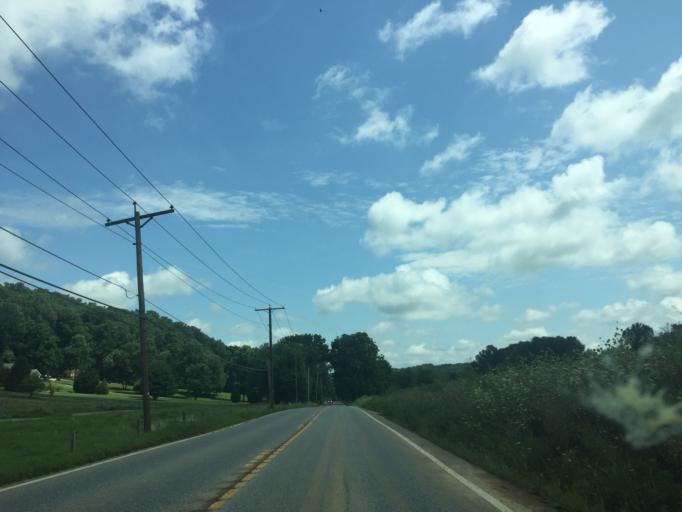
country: US
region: Maryland
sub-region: Baltimore County
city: Perry Hall
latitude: 39.4430
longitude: -76.4789
